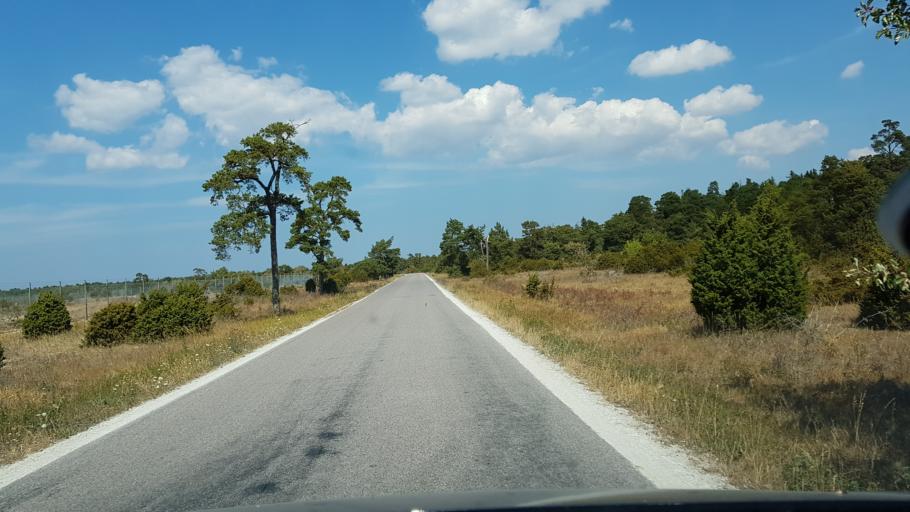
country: SE
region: Gotland
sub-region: Gotland
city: Visby
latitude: 57.6779
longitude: 18.3625
